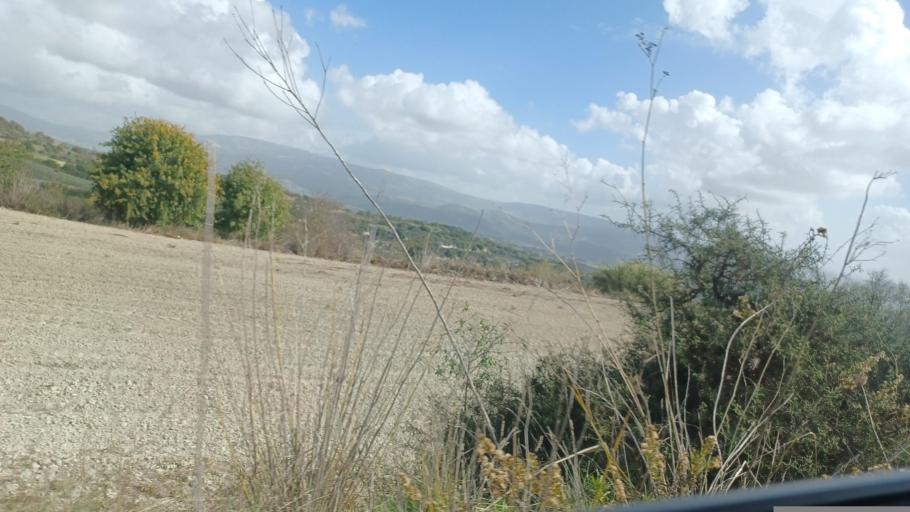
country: CY
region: Pafos
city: Mesogi
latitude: 34.8802
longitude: 32.5109
